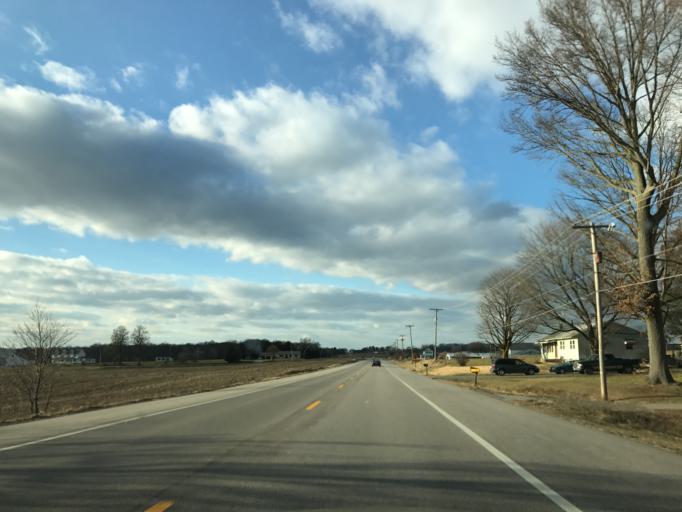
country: US
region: Maryland
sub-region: Cecil County
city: Rising Sun
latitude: 39.6714
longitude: -76.0203
